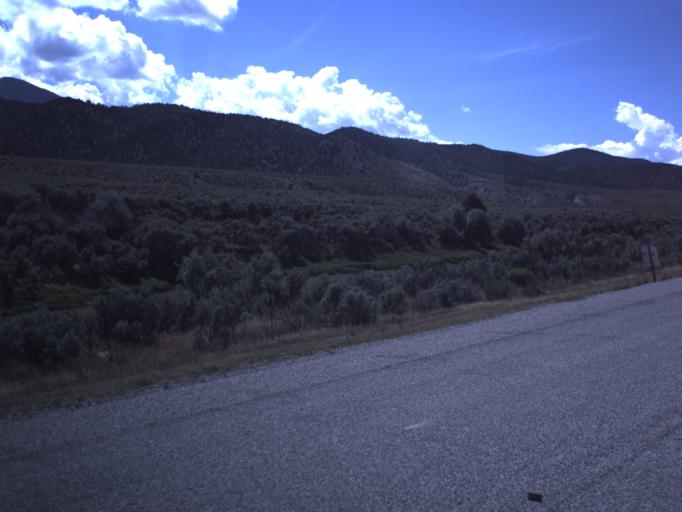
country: US
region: Utah
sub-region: Piute County
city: Junction
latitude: 38.0510
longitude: -112.3533
